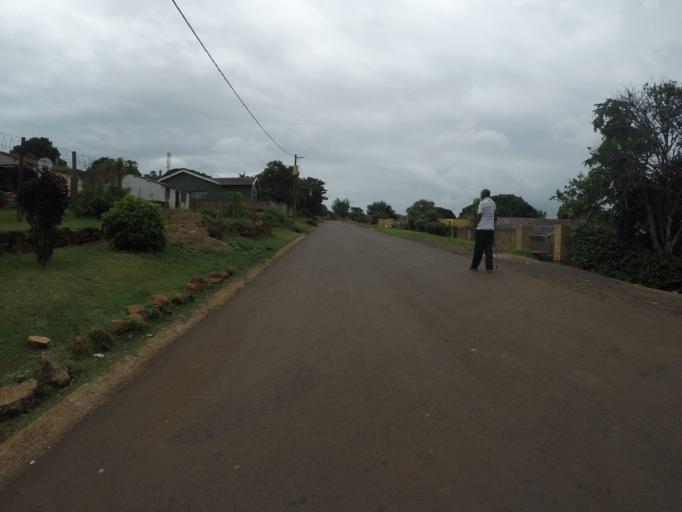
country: ZA
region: KwaZulu-Natal
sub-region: uThungulu District Municipality
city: Empangeni
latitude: -28.7672
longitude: 31.8619
